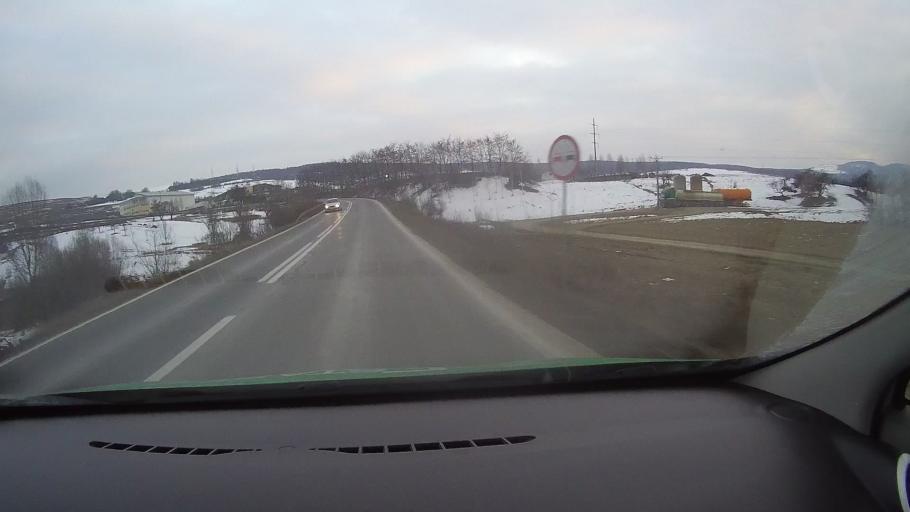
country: RO
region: Harghita
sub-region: Comuna Lupeni
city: Lupeni
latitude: 46.3571
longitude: 25.2391
